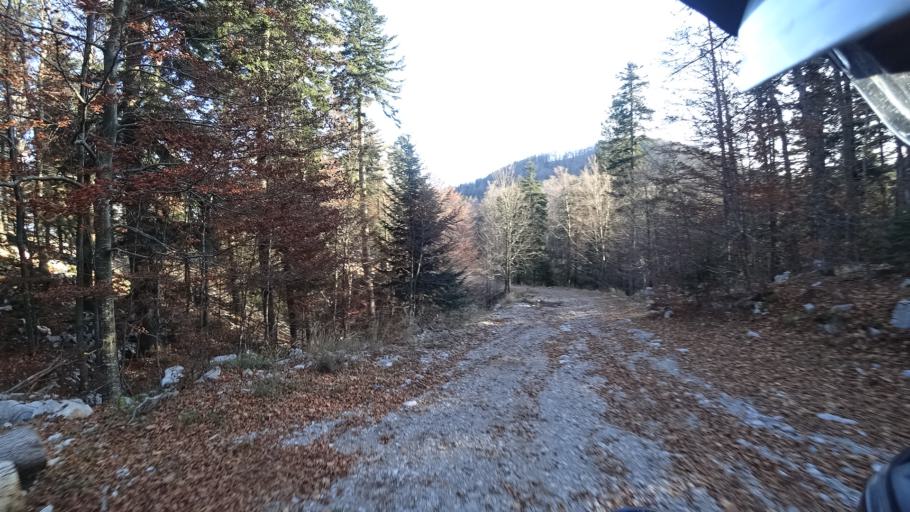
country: HR
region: Primorsko-Goranska
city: Klana
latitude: 45.4813
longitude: 14.4523
